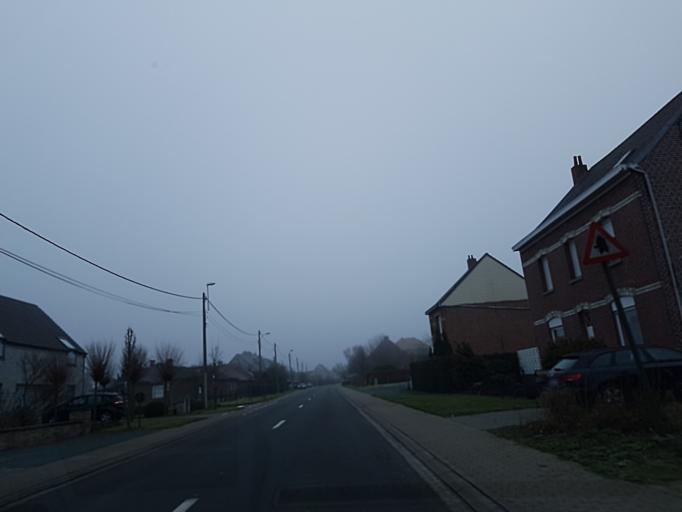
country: BE
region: Flanders
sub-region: Provincie Vlaams-Brabant
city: Meise
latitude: 50.9618
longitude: 4.3204
